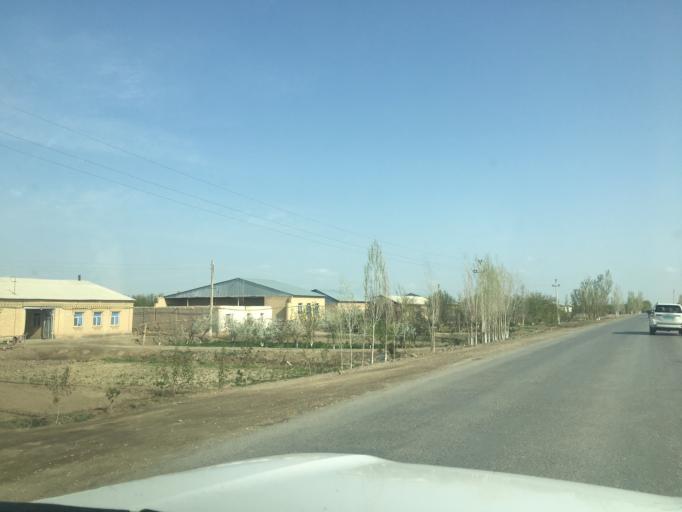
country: TM
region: Lebap
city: Farap
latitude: 39.2020
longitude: 63.5630
